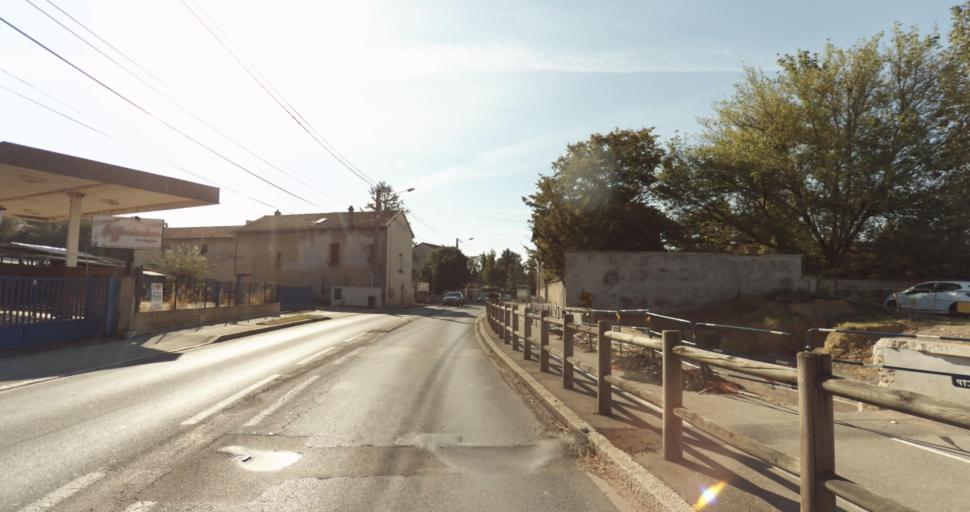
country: FR
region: Rhone-Alpes
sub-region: Departement du Rhone
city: Genay
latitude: 45.8856
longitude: 4.8325
